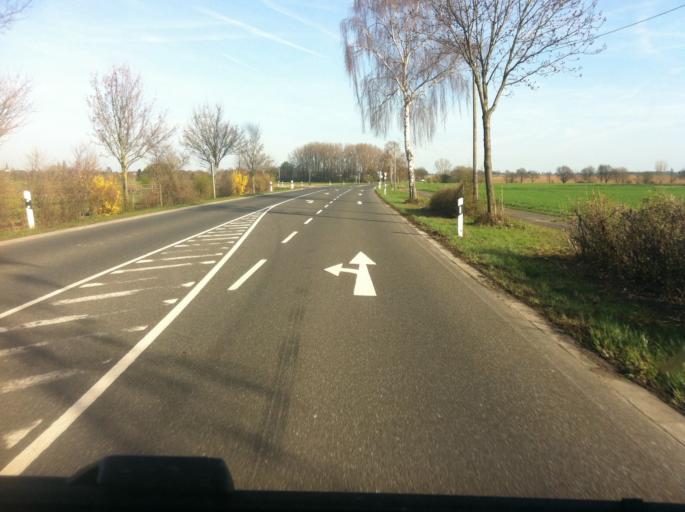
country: DE
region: North Rhine-Westphalia
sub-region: Regierungsbezirk Koln
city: Norvenich
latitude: 50.7650
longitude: 6.7030
